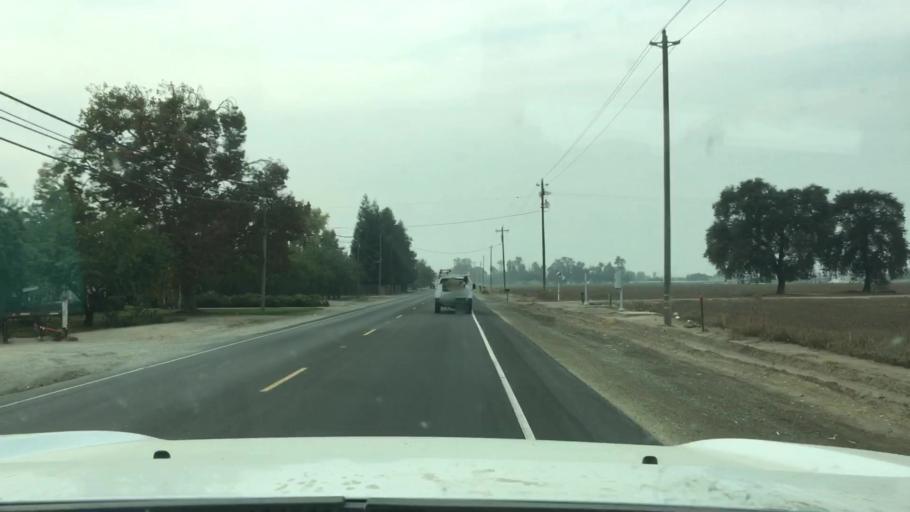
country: US
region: California
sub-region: San Joaquin County
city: French Camp
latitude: 37.8681
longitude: -121.2429
